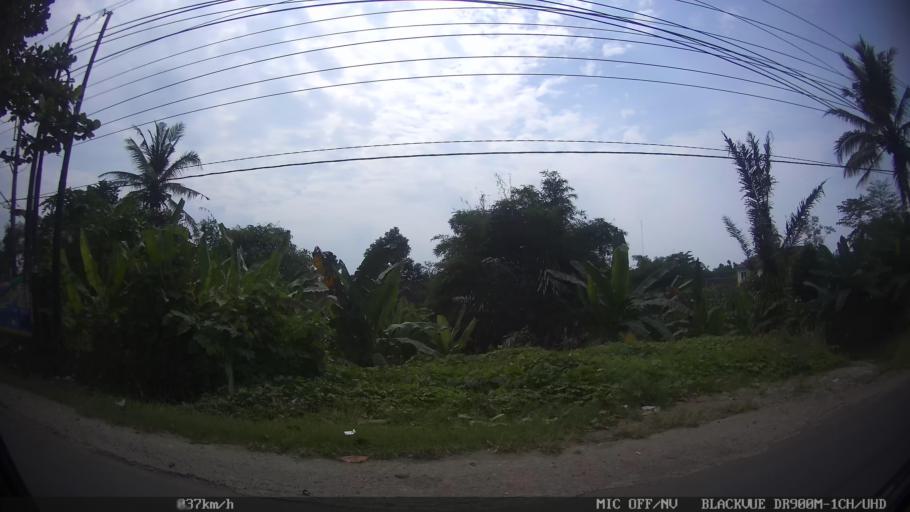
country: ID
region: Lampung
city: Bandarlampung
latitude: -5.4688
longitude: 105.2449
